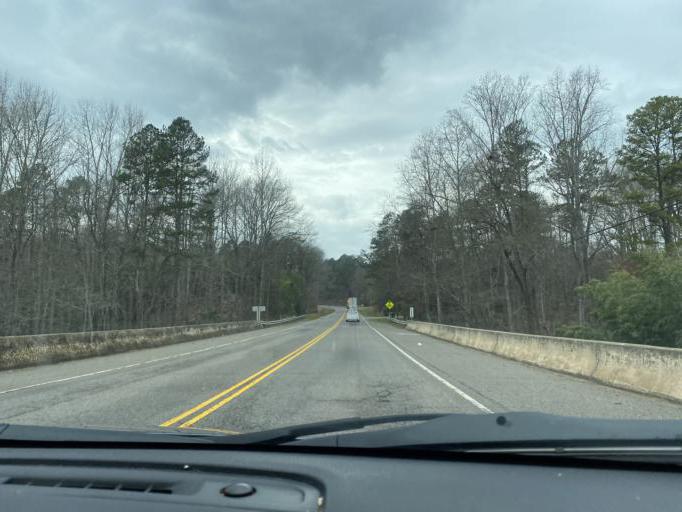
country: US
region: South Carolina
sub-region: Spartanburg County
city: Cowpens
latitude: 35.0169
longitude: -81.7419
